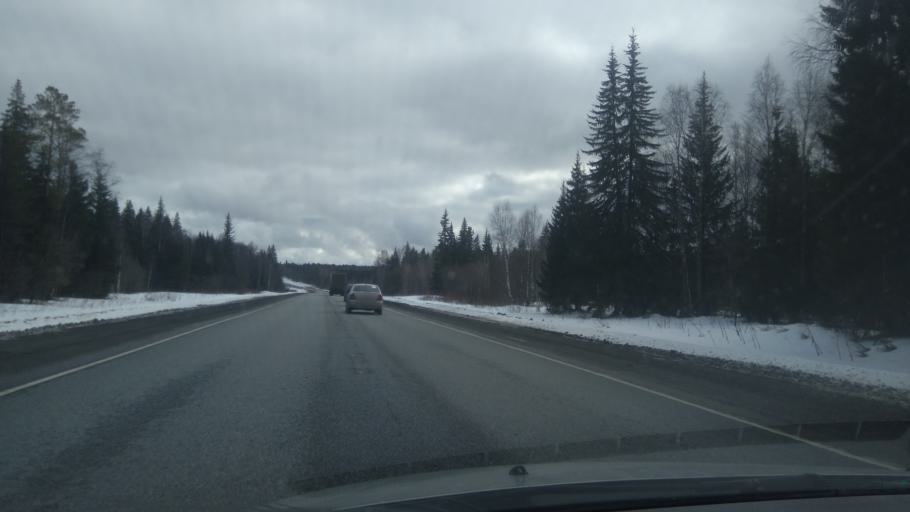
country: RU
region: Sverdlovsk
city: Atig
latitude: 56.8088
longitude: 59.3670
